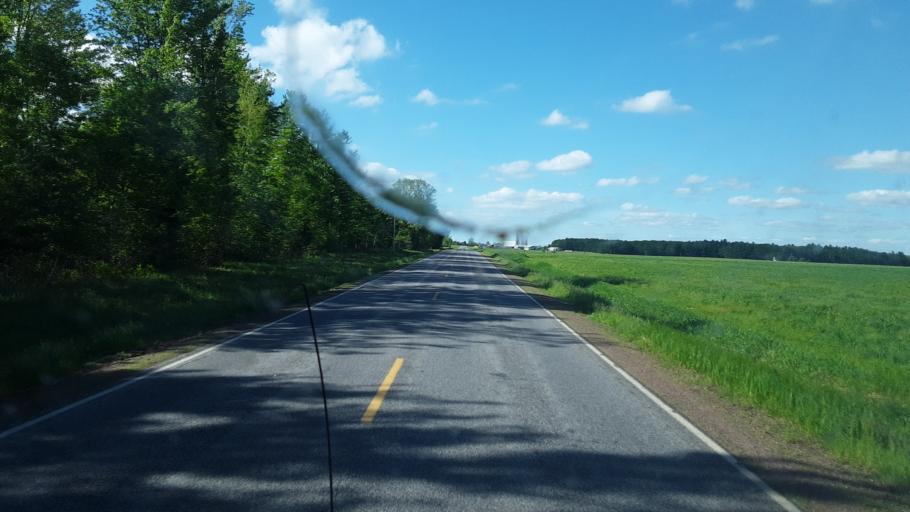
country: US
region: Wisconsin
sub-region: Wood County
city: Marshfield
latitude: 44.4147
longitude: -90.1602
